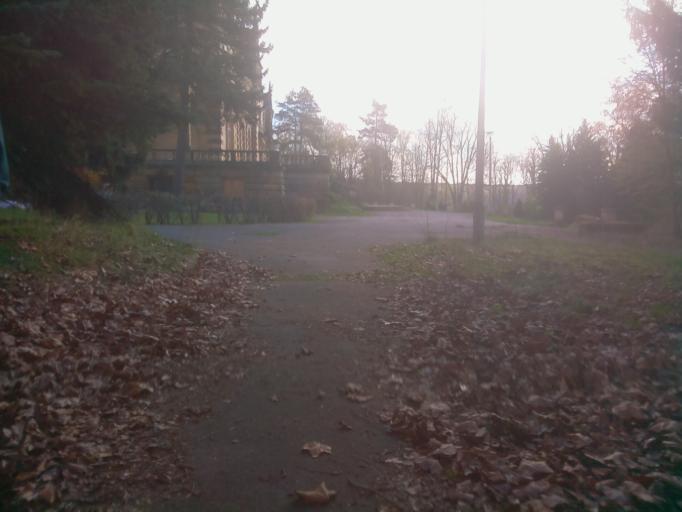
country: DE
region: Thuringia
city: Hummelshain
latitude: 50.7699
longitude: 11.6265
